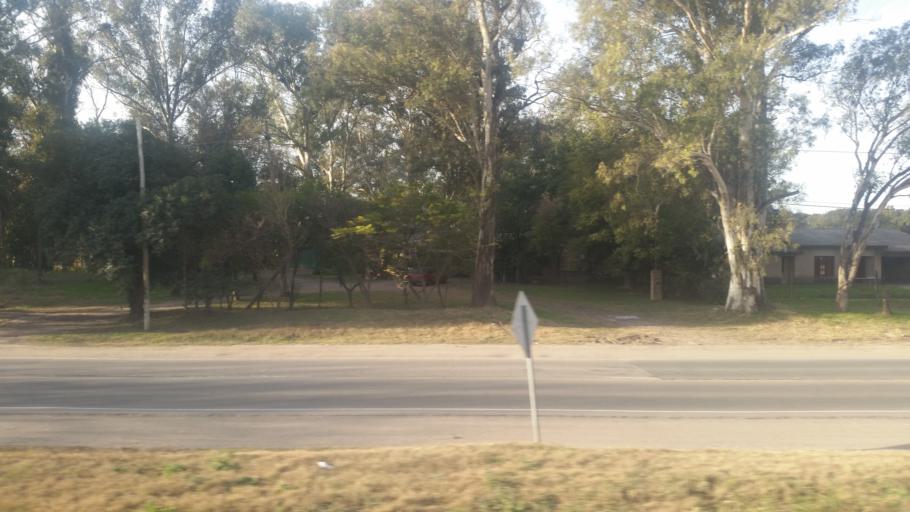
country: AR
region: Cordoba
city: Toledo
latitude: -31.4897
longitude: -64.0776
